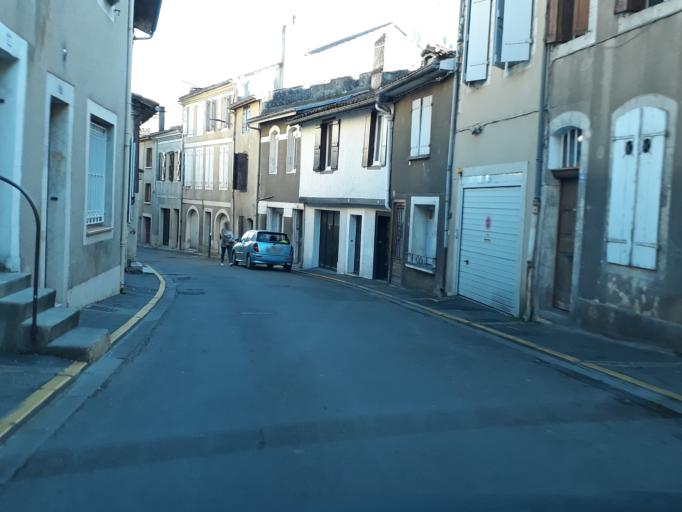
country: FR
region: Midi-Pyrenees
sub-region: Departement du Gers
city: Auch
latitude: 43.6444
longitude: 0.5852
